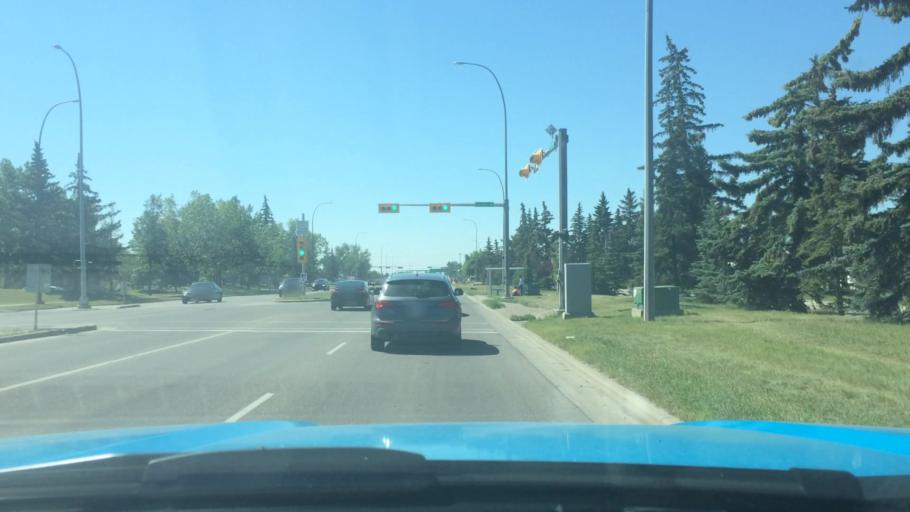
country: CA
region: Alberta
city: Calgary
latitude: 51.0743
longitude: -113.9585
